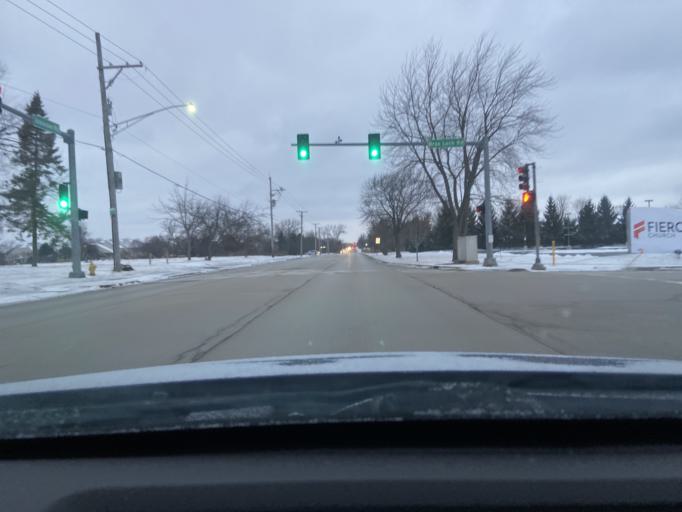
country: US
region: Illinois
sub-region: Lake County
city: Grayslake
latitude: 42.3515
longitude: -88.0240
